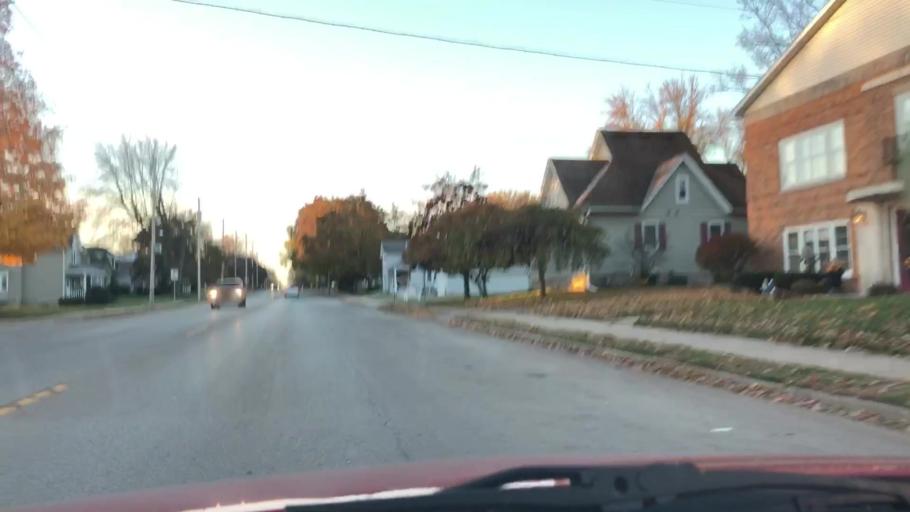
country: US
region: Wisconsin
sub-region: Outagamie County
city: Seymour
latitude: 44.5095
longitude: -88.3304
